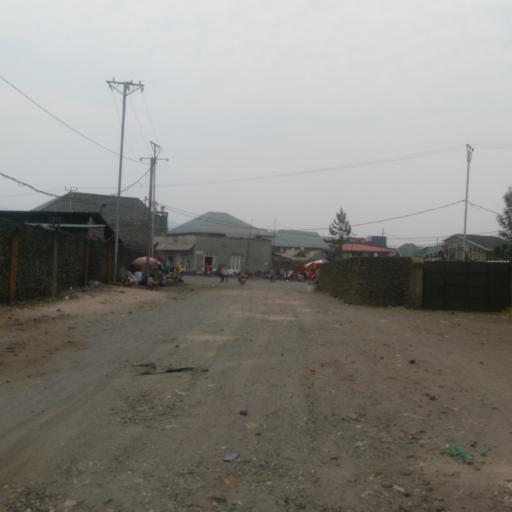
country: CD
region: Nord Kivu
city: Goma
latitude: -1.6847
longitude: 29.2337
